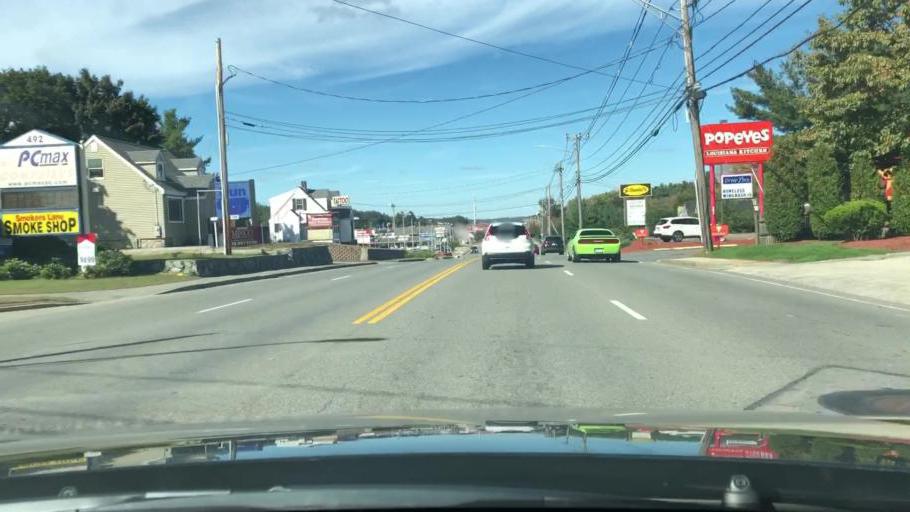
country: US
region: Massachusetts
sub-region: Essex County
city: Methuen
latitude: 42.7445
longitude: -71.2005
